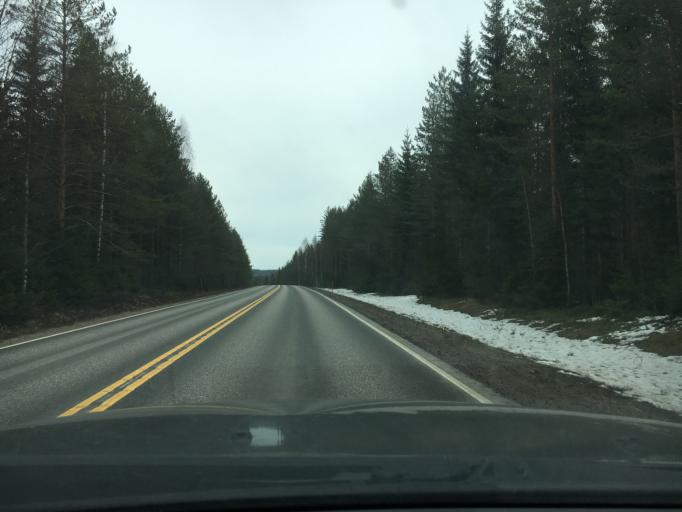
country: FI
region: Central Finland
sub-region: AEaenekoski
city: Sumiainen
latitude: 62.5555
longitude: 26.0236
